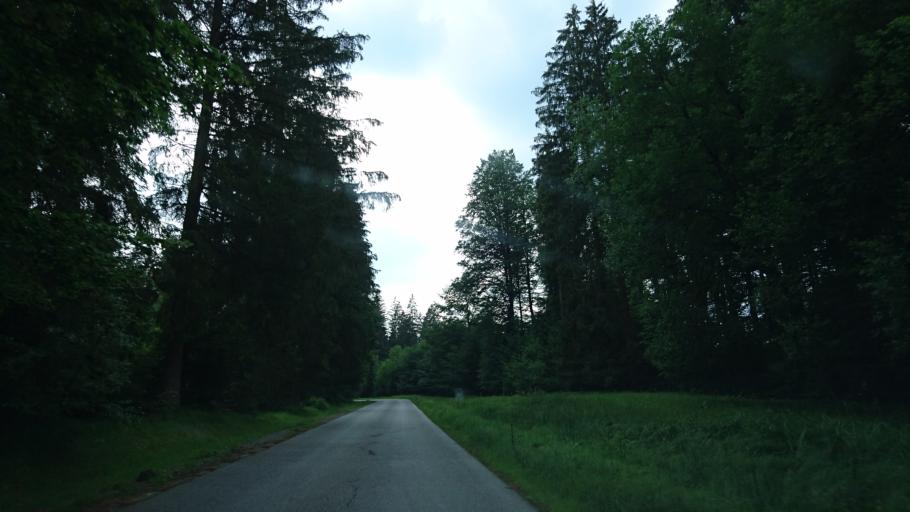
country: DE
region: Bavaria
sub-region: Lower Bavaria
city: Spiegelau
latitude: 48.9438
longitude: 13.3332
